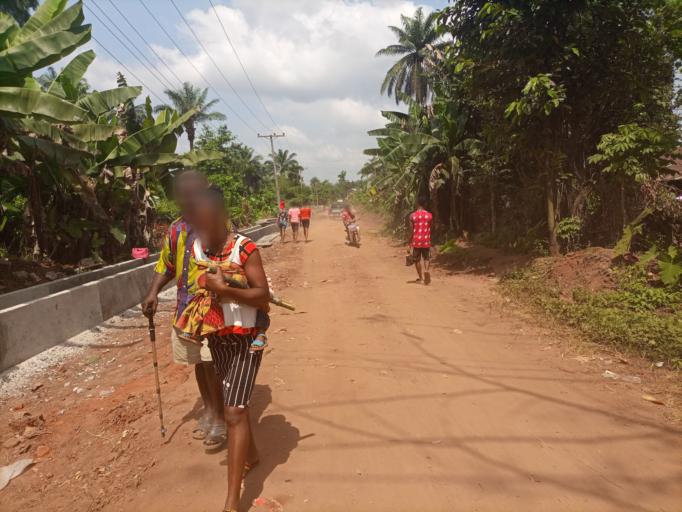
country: NG
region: Imo
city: Ihuo
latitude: 5.5259
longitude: 7.2628
